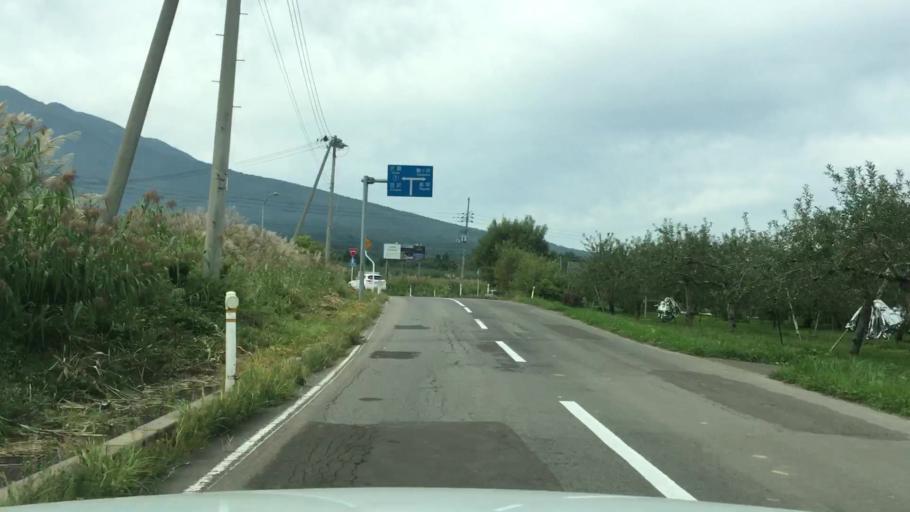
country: JP
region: Aomori
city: Hirosaki
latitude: 40.6779
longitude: 140.3745
